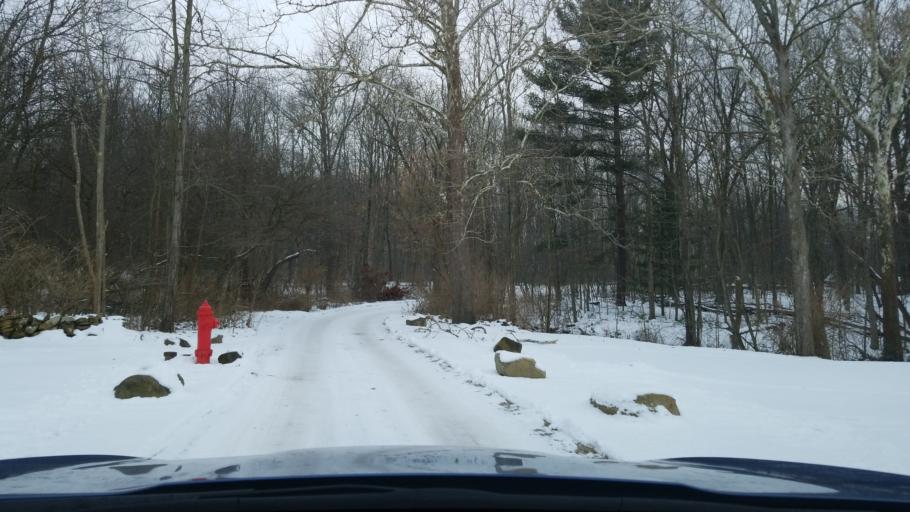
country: US
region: Ohio
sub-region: Cuyahoga County
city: Brecksville
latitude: 41.3156
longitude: -81.5773
